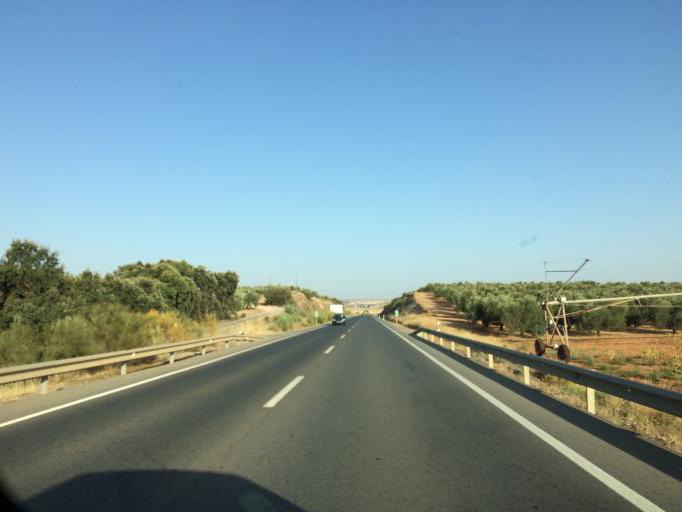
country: ES
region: Andalusia
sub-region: Provincia de Malaga
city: Humilladero
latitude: 37.0587
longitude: -4.6851
